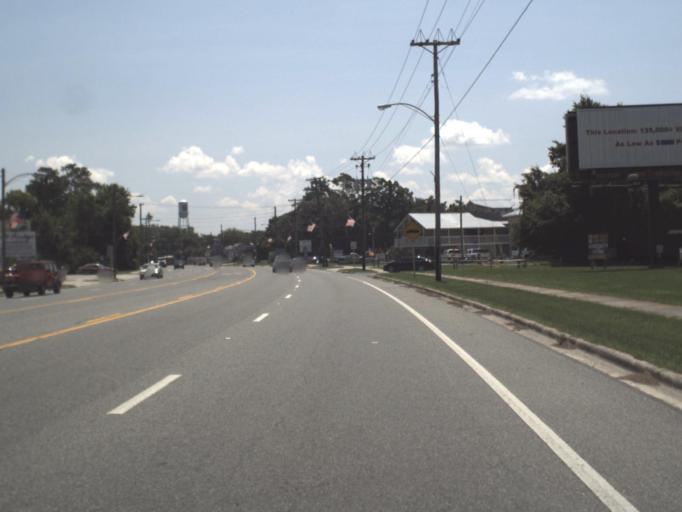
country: US
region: Florida
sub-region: Citrus County
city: Crystal River
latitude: 28.9001
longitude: -82.5979
